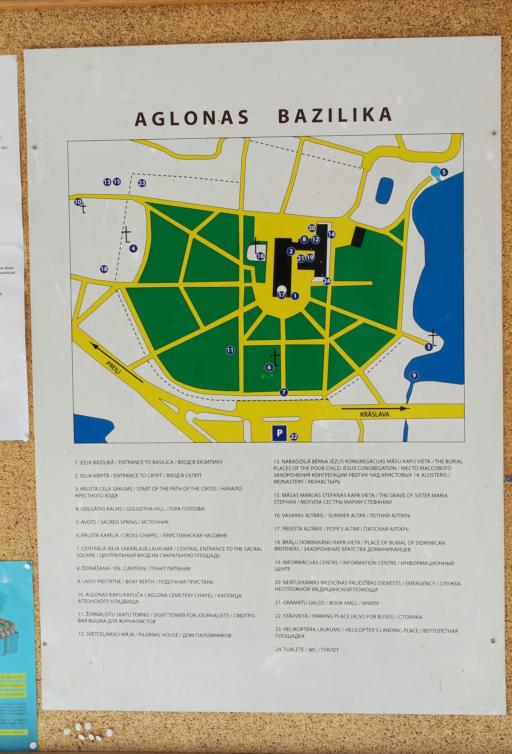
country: LV
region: Aglona
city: Aglona
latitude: 56.1272
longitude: 27.0160
